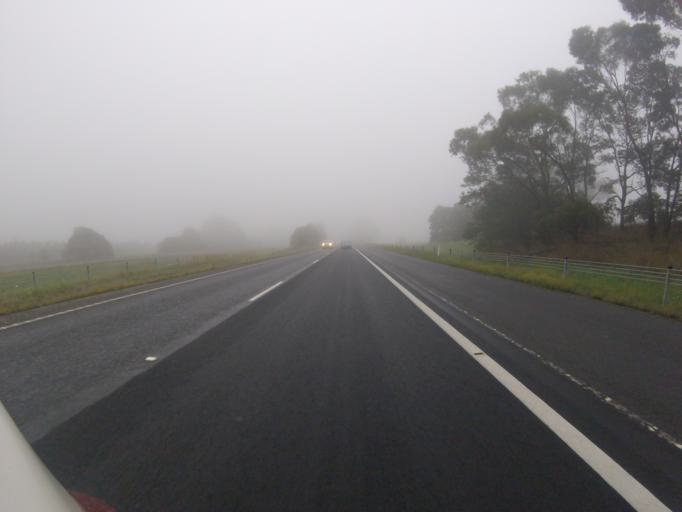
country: AU
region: Victoria
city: Brown Hill
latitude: -37.5497
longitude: 144.0330
